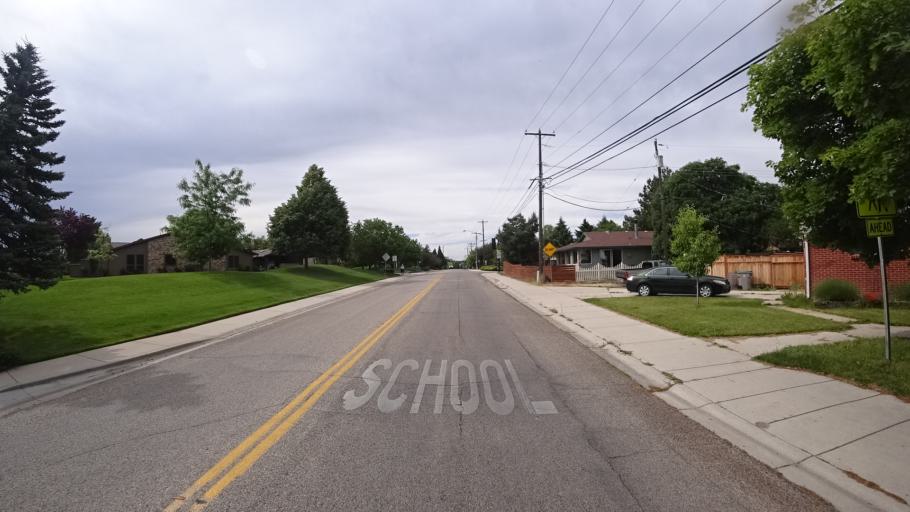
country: US
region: Idaho
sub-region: Ada County
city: Boise
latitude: 43.5772
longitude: -116.2236
